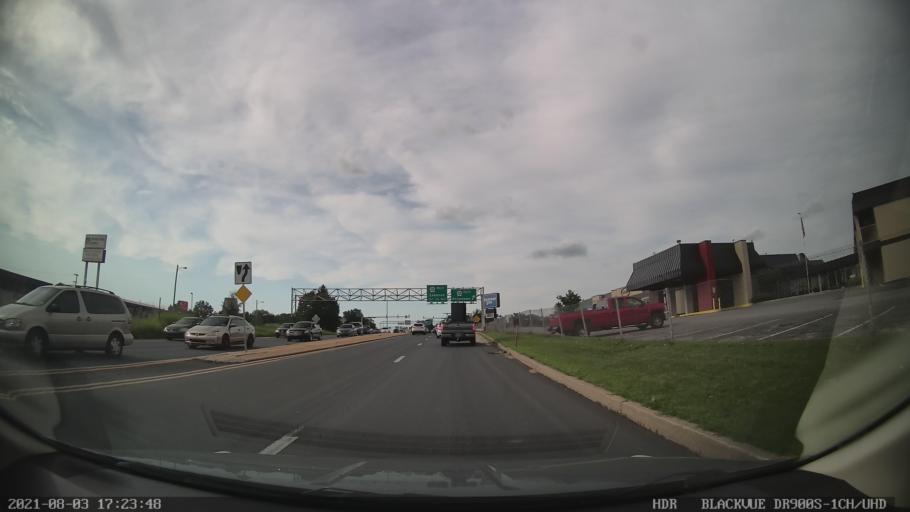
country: US
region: Pennsylvania
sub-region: Berks County
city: Hyde Park
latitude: 40.3695
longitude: -75.9267
